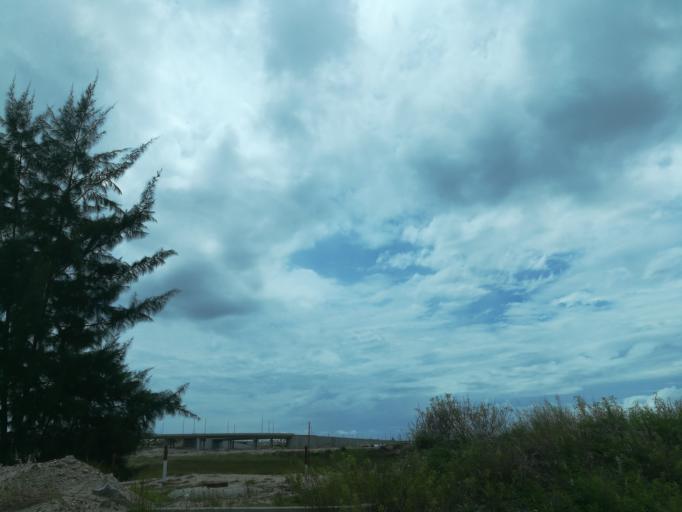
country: NG
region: Lagos
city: Lagos
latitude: 6.4139
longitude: 3.4076
